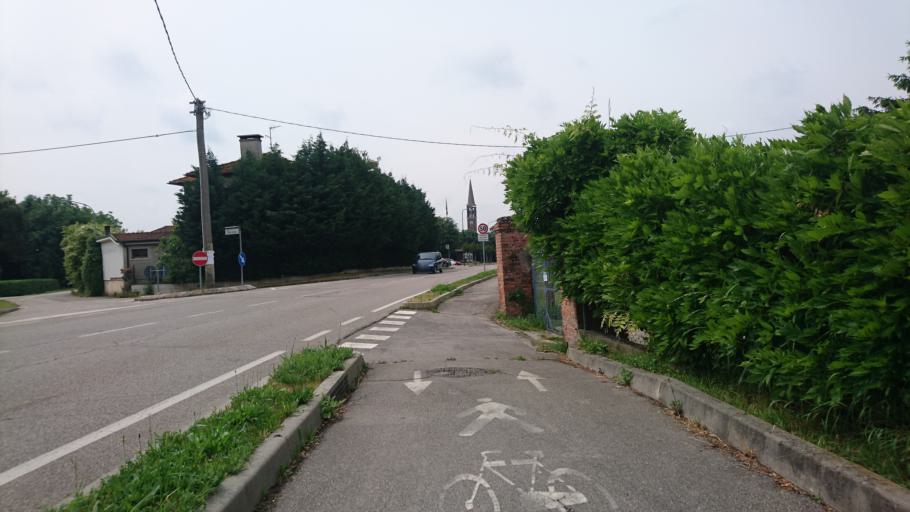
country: IT
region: Veneto
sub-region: Provincia di Rovigo
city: Lendinara
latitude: 45.1142
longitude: 11.6205
